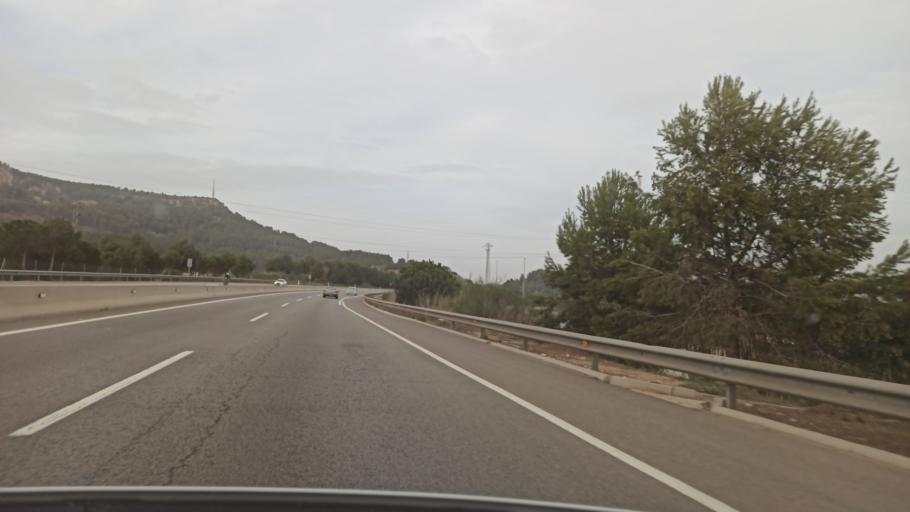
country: ES
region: Catalonia
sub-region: Provincia de Barcelona
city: Palleja
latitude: 41.4034
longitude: 1.9864
